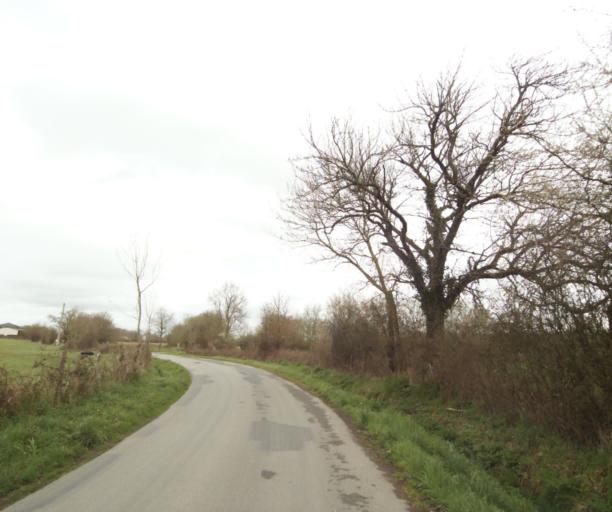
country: FR
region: Pays de la Loire
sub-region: Departement de la Loire-Atlantique
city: Bouvron
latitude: 47.4280
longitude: -1.8983
